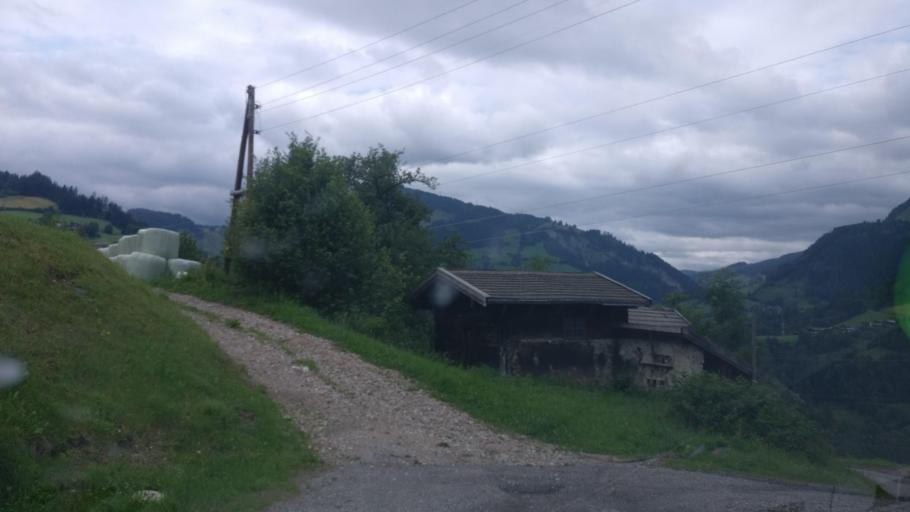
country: AT
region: Salzburg
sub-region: Politischer Bezirk Zell am See
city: Lend
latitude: 47.2933
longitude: 13.0422
